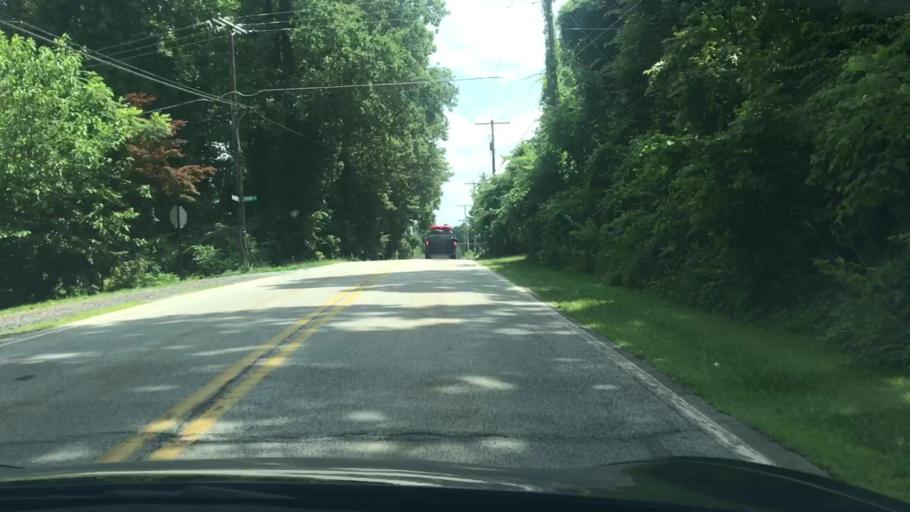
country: US
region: Pennsylvania
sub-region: York County
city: Valley Green
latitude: 40.1158
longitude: -76.7762
